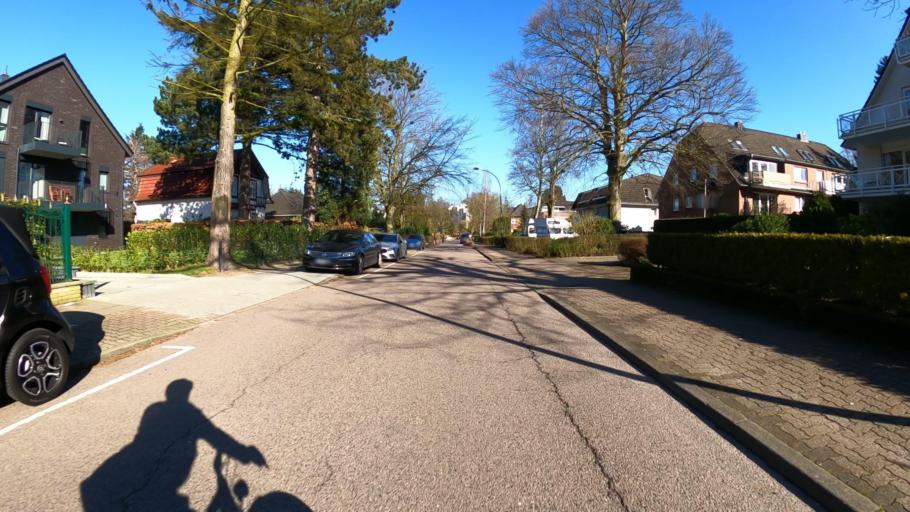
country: DE
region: Schleswig-Holstein
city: Rellingen
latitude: 53.6485
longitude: 9.7981
